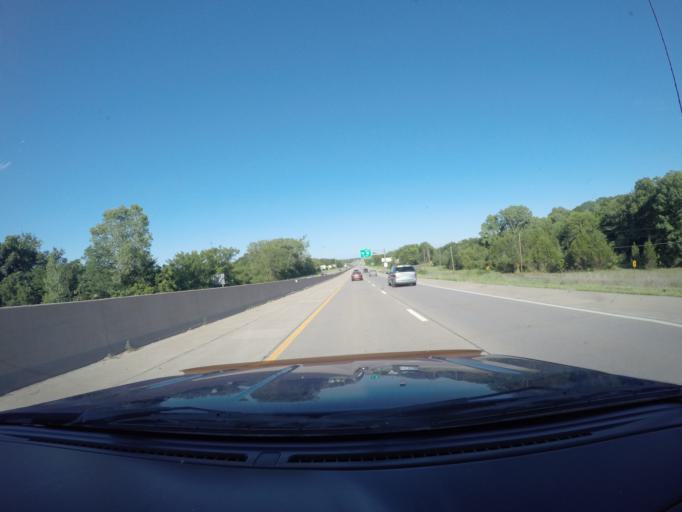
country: US
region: Kansas
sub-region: Shawnee County
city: Silver Lake
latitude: 39.0533
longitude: -95.7888
